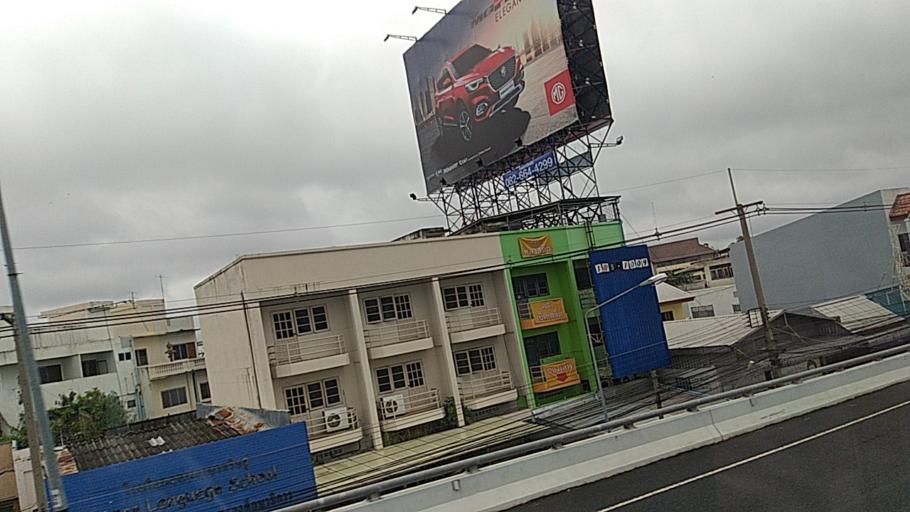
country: TH
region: Nakhon Ratchasima
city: Nakhon Ratchasima
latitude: 15.0281
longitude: 102.1388
